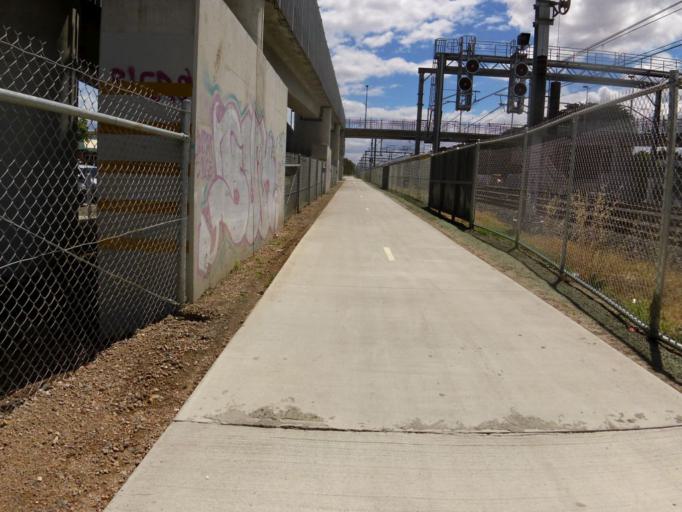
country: AU
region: Victoria
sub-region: Greater Dandenong
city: Springvale
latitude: -37.9462
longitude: 145.1489
